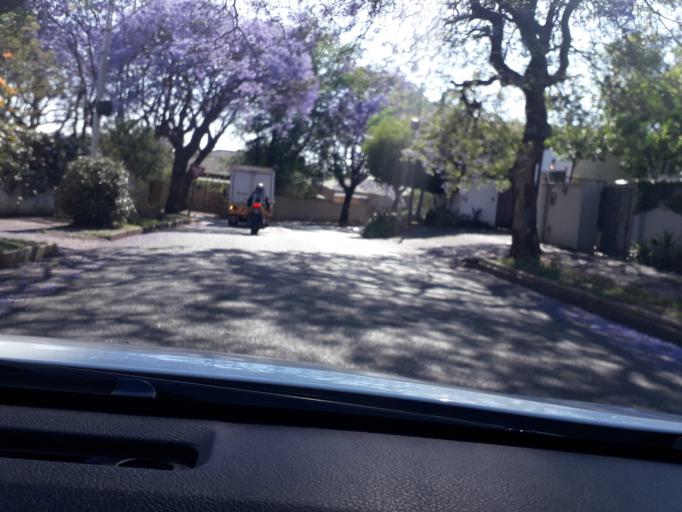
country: ZA
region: Gauteng
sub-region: City of Johannesburg Metropolitan Municipality
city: Johannesburg
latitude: -26.1775
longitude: 28.0056
